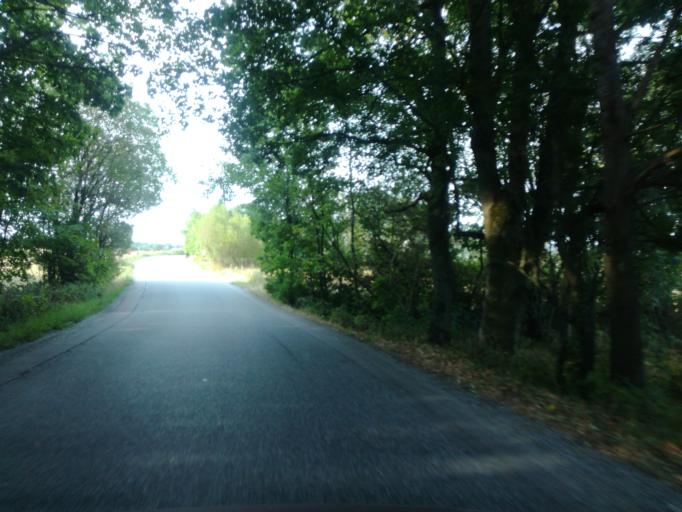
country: DK
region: South Denmark
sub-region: Vejle Kommune
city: Vejle
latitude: 55.6590
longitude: 9.5465
